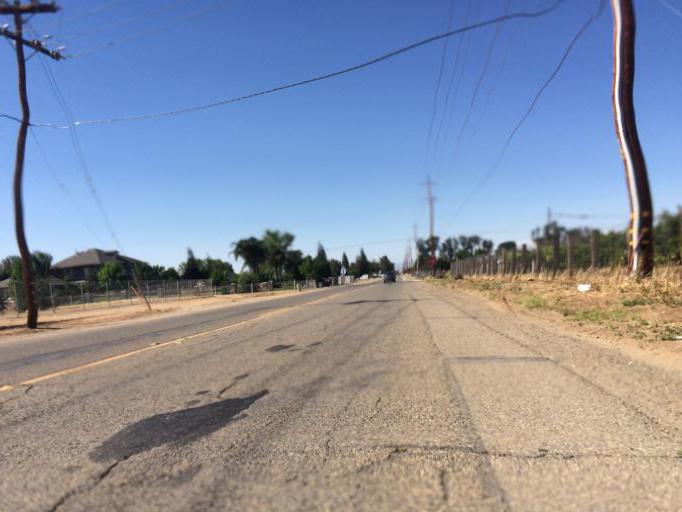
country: US
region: California
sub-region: Fresno County
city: Sanger
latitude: 36.7640
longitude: -119.6101
